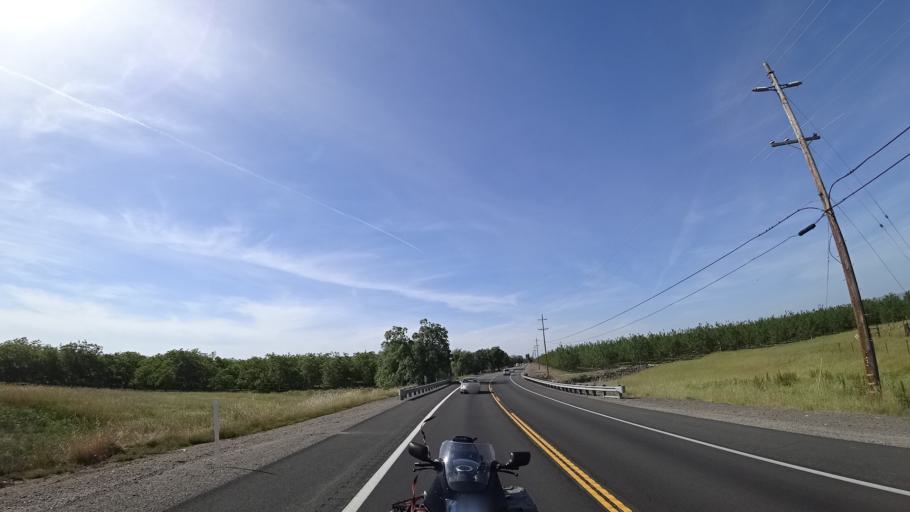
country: US
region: California
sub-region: Glenn County
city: Hamilton City
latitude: 39.8701
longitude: -121.9666
